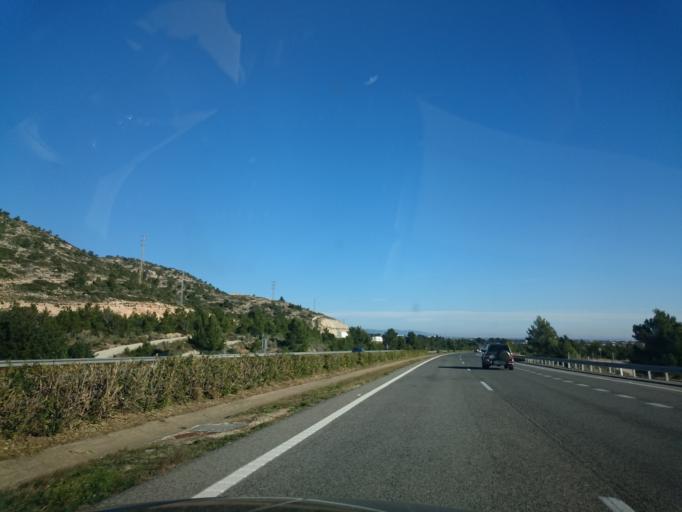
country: ES
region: Catalonia
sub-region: Provincia de Tarragona
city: Colldejou
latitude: 40.9886
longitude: 0.8992
